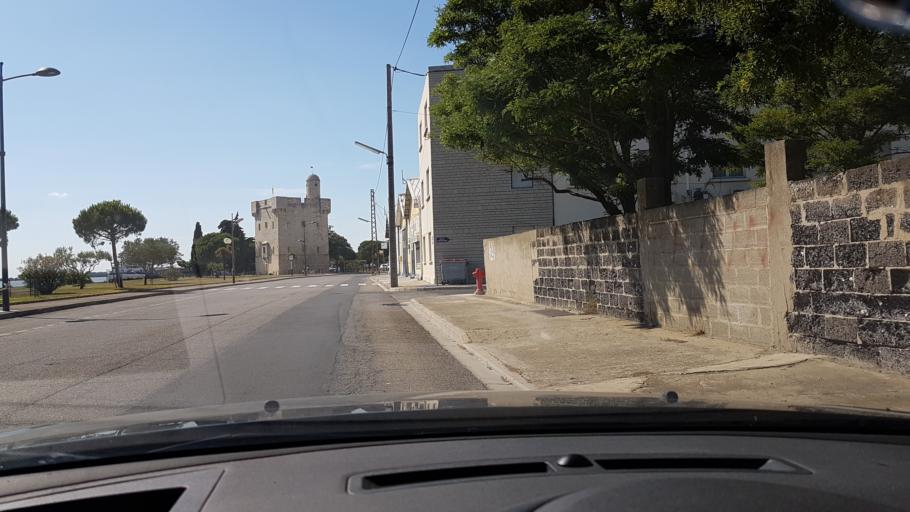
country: FR
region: Provence-Alpes-Cote d'Azur
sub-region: Departement des Bouches-du-Rhone
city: Port-Saint-Louis-du-Rhone
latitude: 43.3839
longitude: 4.8063
